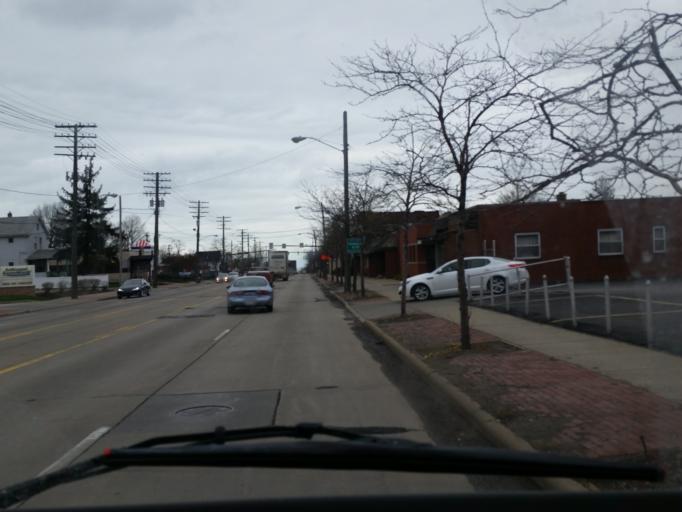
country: US
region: Ohio
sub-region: Cuyahoga County
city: Lakewood
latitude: 41.4779
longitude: -81.7687
